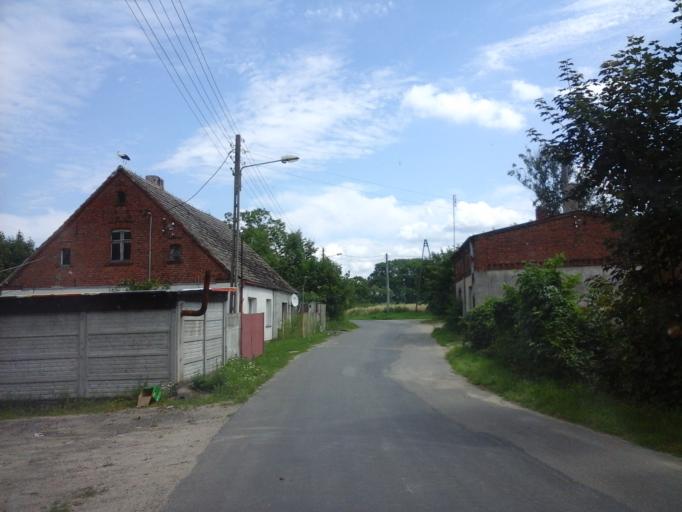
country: PL
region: West Pomeranian Voivodeship
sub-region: Powiat choszczenski
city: Recz
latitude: 53.2919
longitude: 15.5008
